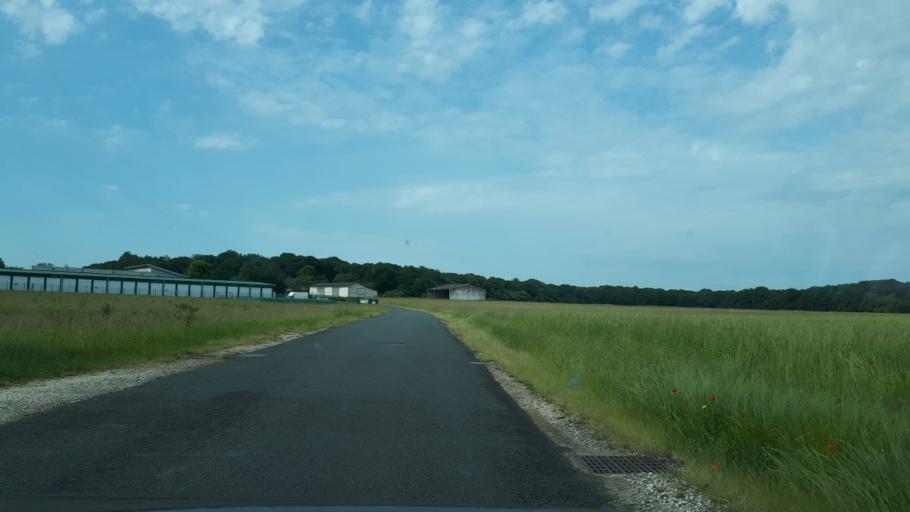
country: FR
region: Centre
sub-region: Departement d'Indre-et-Loire
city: Monnaie
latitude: 47.4960
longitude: 0.7768
